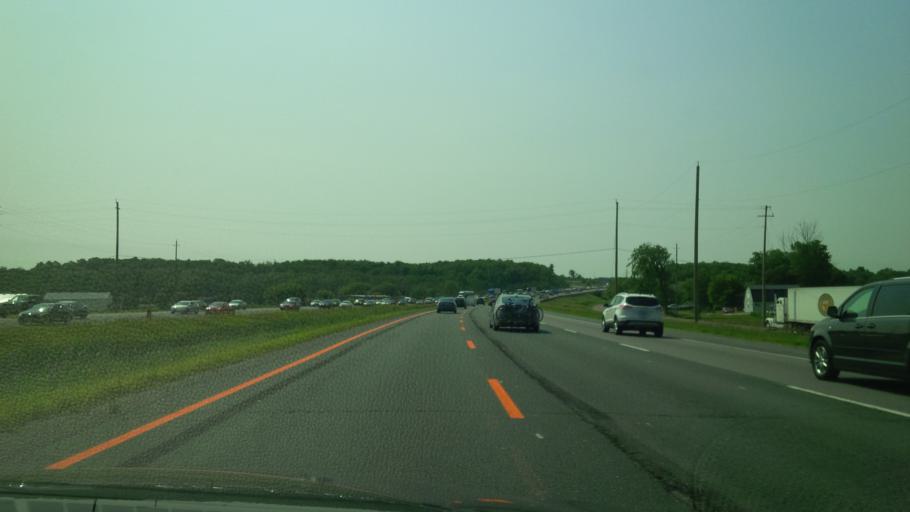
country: CA
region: Ontario
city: Bradford West Gwillimbury
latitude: 44.0387
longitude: -79.5979
